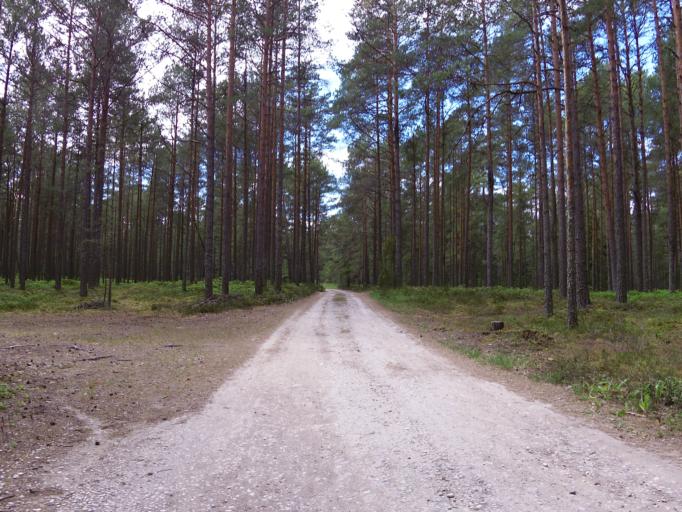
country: EE
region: Harju
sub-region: Paldiski linn
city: Paldiski
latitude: 59.2487
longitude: 23.7493
